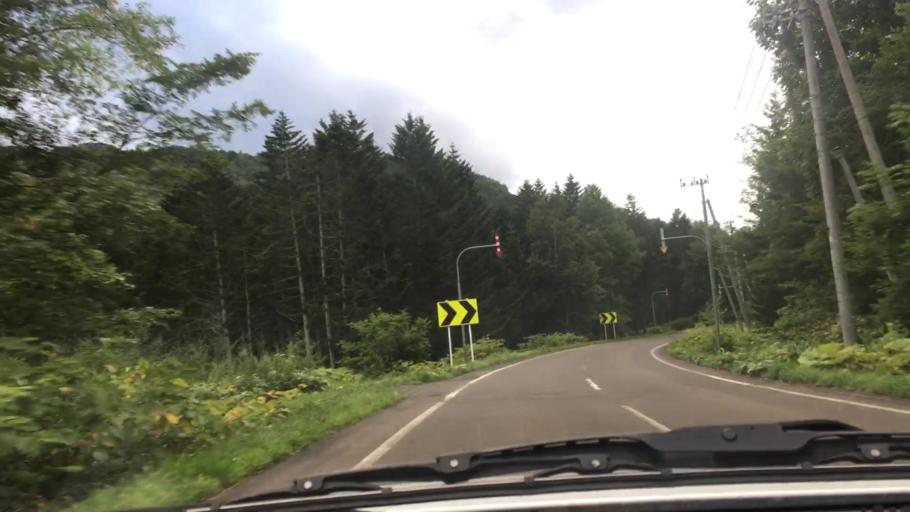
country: JP
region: Hokkaido
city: Shimo-furano
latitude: 43.0440
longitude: 142.5195
